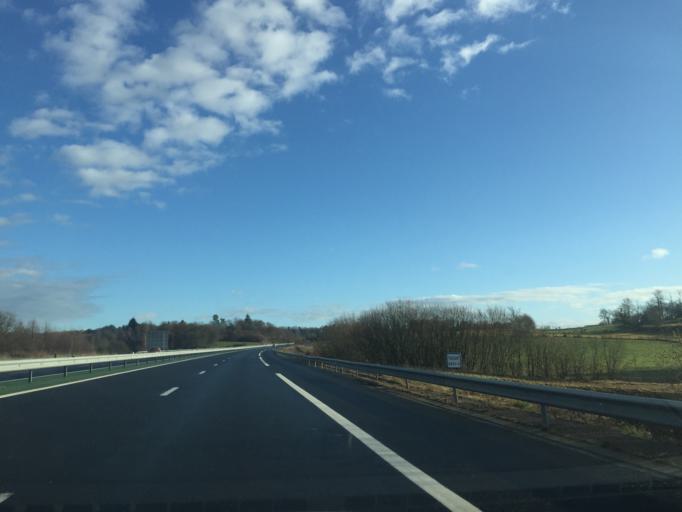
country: FR
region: Limousin
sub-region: Departement de la Correze
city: Saint-Mexant
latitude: 45.3047
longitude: 1.6588
